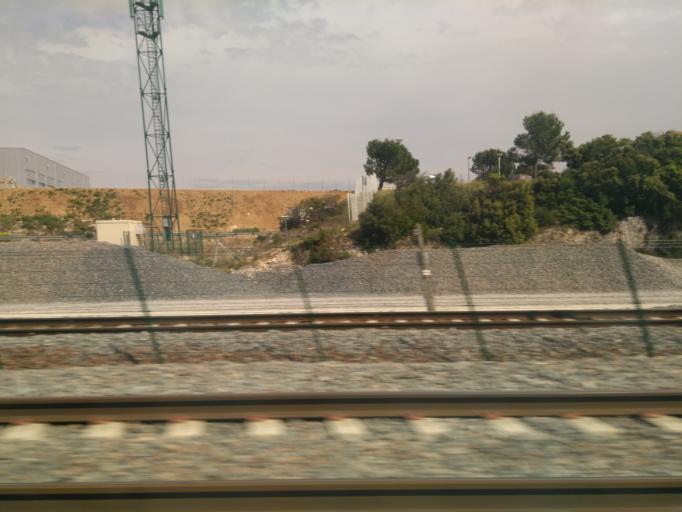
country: FR
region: Languedoc-Roussillon
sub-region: Departement du Gard
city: Pujaut
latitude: 44.0166
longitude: 4.7415
